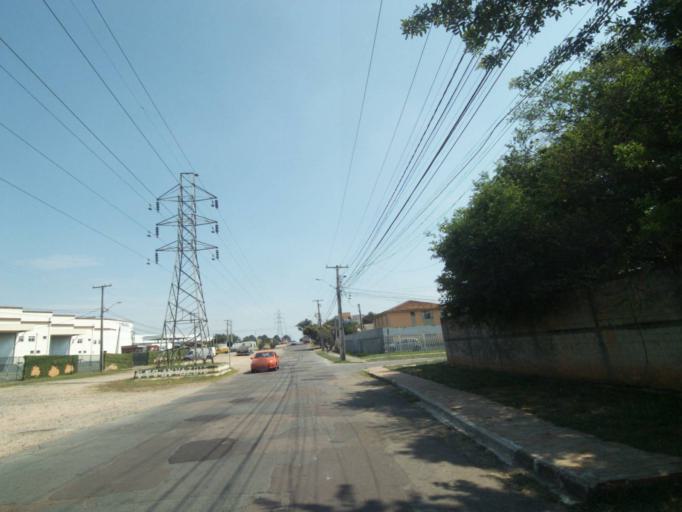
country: BR
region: Parana
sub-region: Curitiba
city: Curitiba
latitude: -25.4793
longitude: -49.3198
